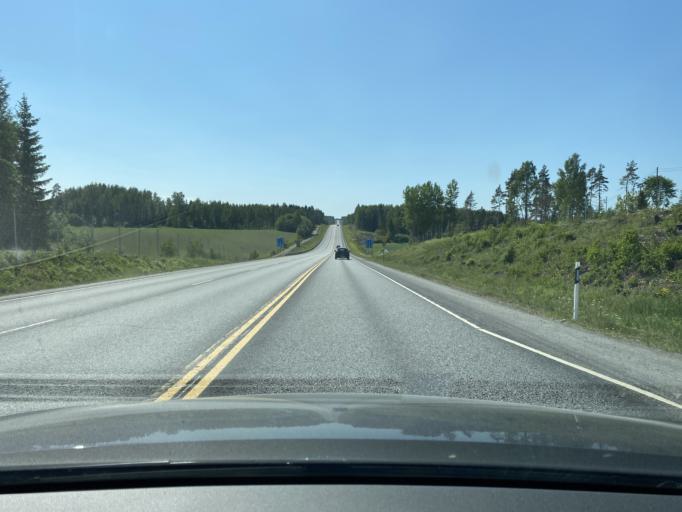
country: FI
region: Pirkanmaa
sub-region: Tampere
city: Nokia
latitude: 61.4052
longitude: 23.2830
